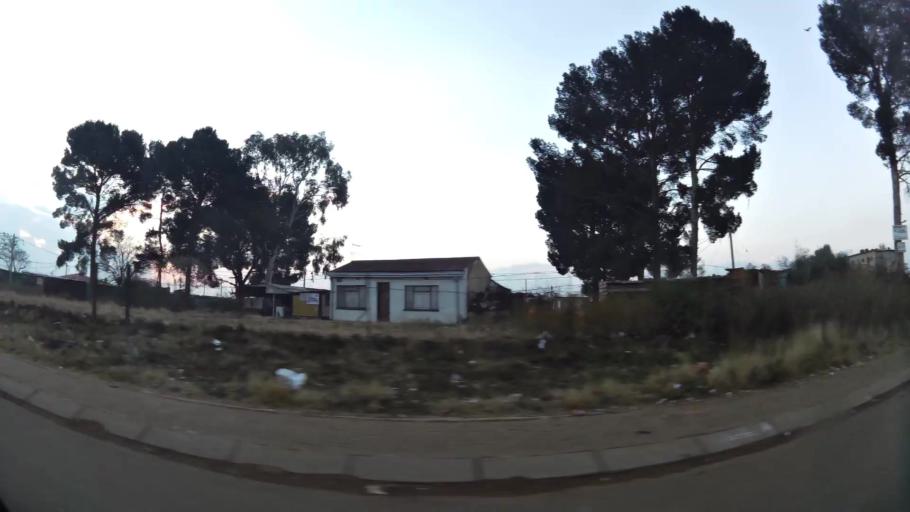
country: ZA
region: Gauteng
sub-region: City of Johannesburg Metropolitan Municipality
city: Orange Farm
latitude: -26.5553
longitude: 27.8796
